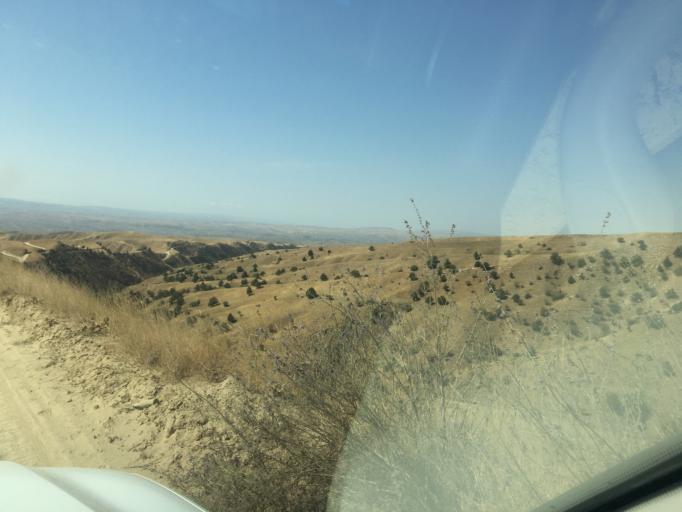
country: TM
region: Ahal
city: Baharly
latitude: 38.2844
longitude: 56.9280
